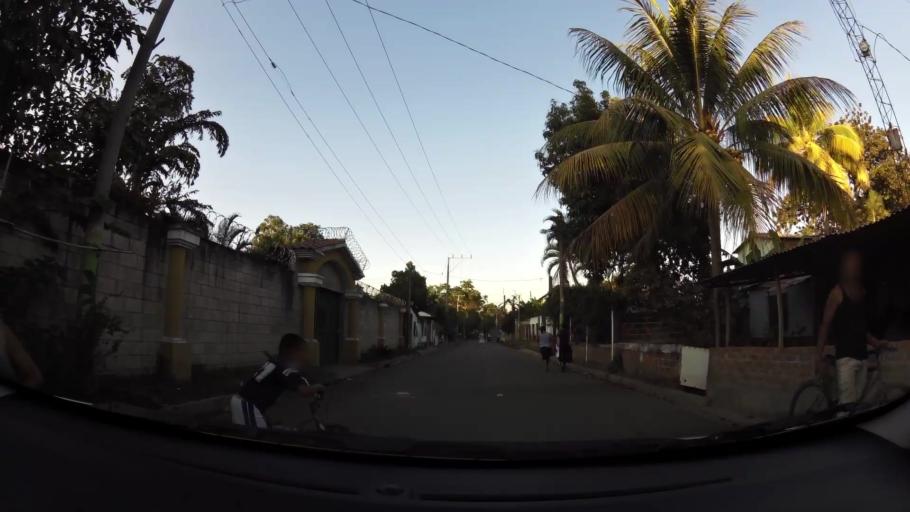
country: SV
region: Sonsonate
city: Armenia
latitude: 13.7414
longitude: -89.4013
